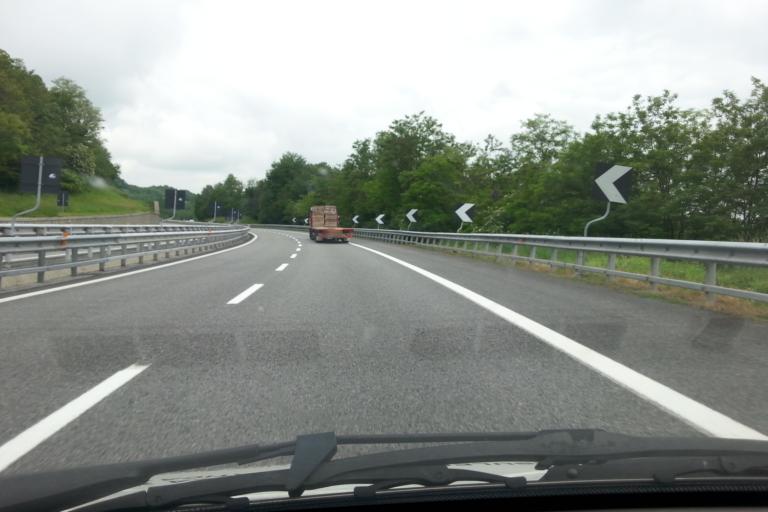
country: IT
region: Piedmont
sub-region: Provincia di Cuneo
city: Niella Tanaro
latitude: 44.4135
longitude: 7.9070
